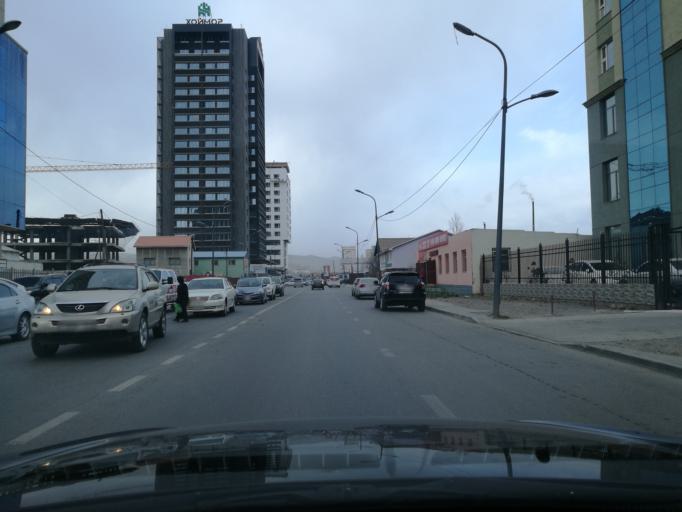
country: MN
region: Ulaanbaatar
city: Ulaanbaatar
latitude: 47.9310
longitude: 106.9140
